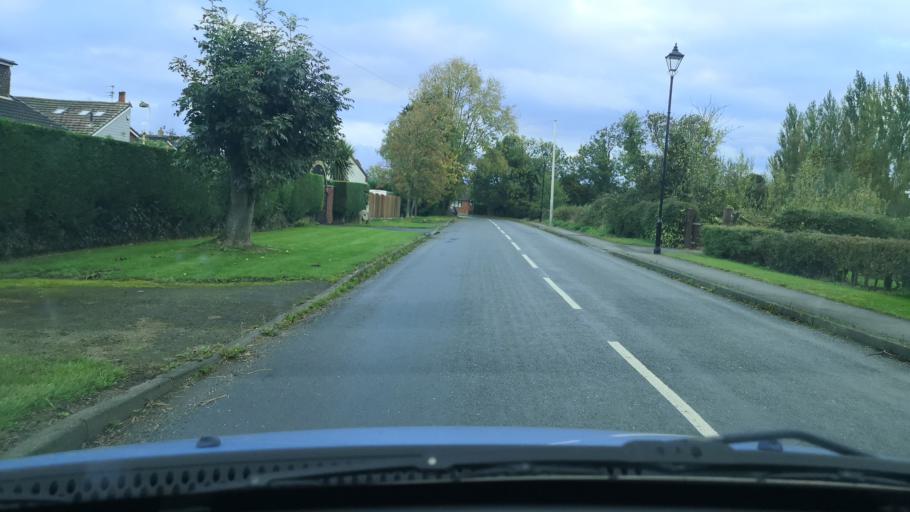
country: GB
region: England
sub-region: Doncaster
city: Stainforth
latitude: 53.6130
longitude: -1.0186
